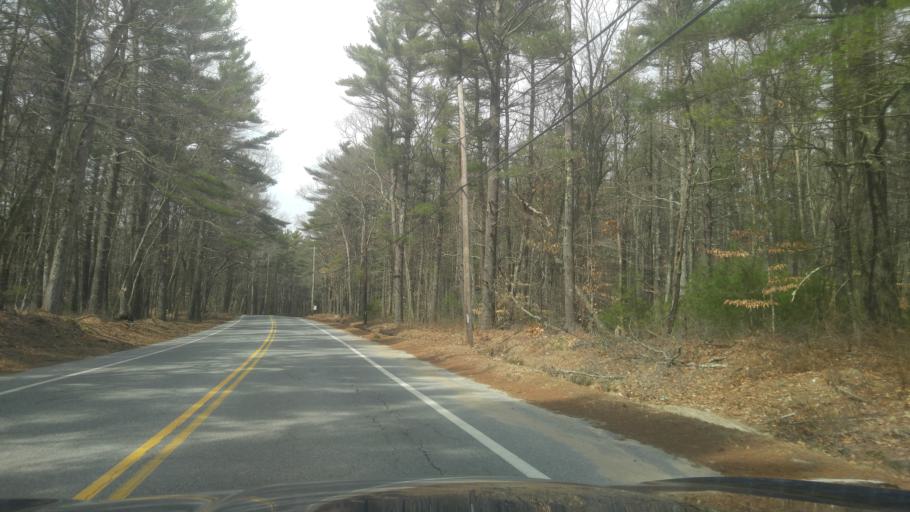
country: US
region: Rhode Island
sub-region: Washington County
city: Exeter
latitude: 41.6315
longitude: -71.5719
